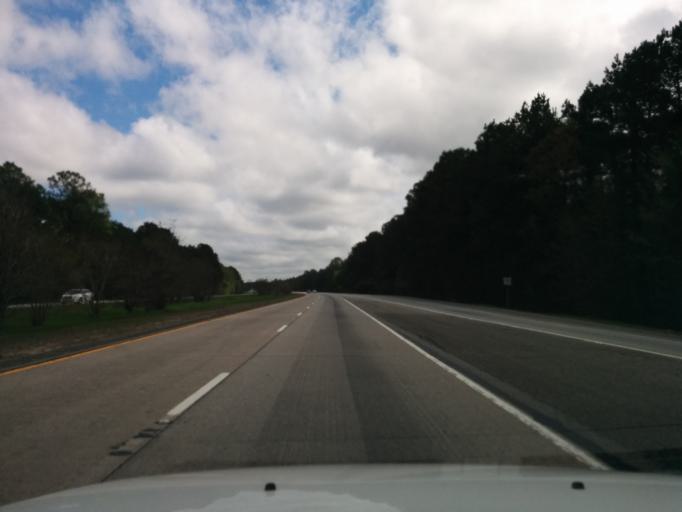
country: US
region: Georgia
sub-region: Chatham County
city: Bloomingdale
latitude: 32.1228
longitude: -81.3843
